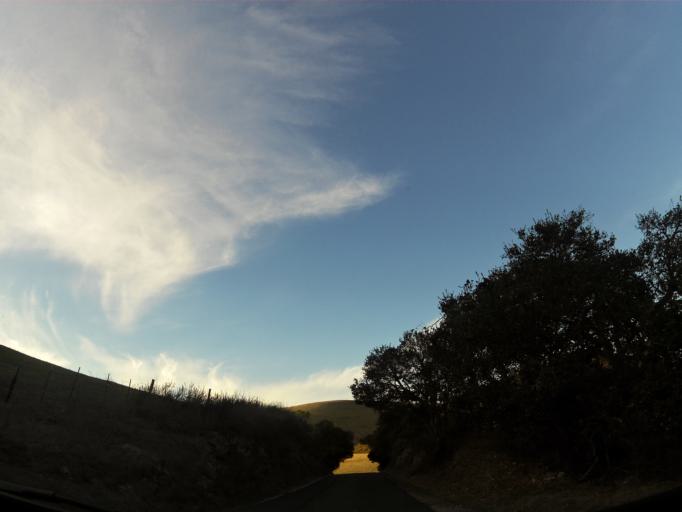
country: US
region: California
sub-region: San Benito County
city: San Juan Bautista
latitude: 36.8149
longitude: -121.5754
